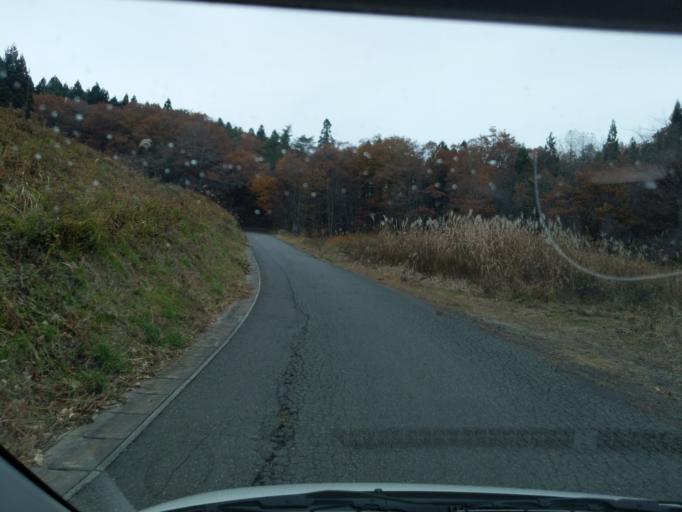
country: JP
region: Iwate
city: Ichinoseki
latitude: 38.9798
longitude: 141.0020
